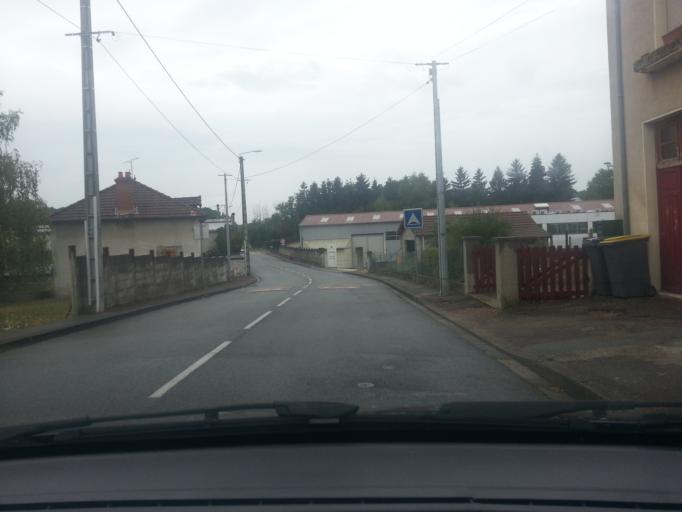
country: FR
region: Bourgogne
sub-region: Departement de Saone-et-Loire
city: Montchanin
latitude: 46.7432
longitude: 4.4646
